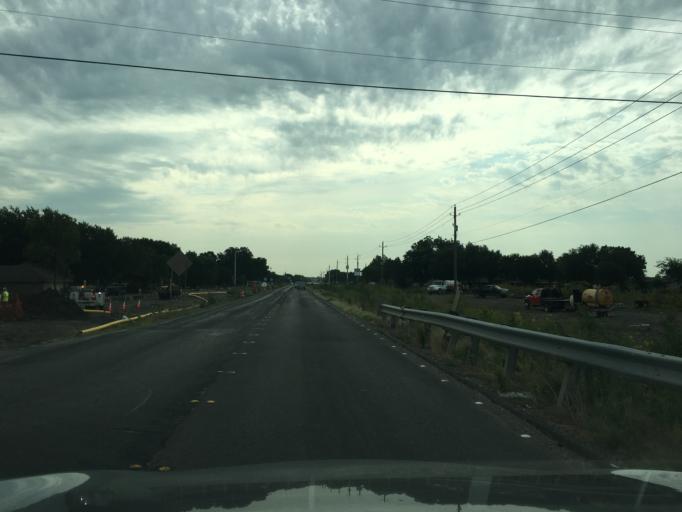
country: US
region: Texas
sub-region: Collin County
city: Parker
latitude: 33.0554
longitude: -96.6008
